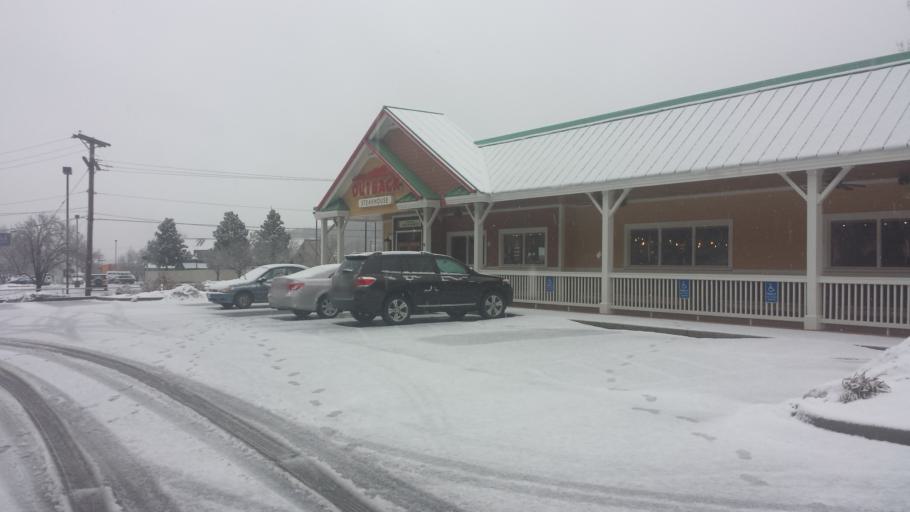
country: US
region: Virginia
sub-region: Roanoke County
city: Narrows
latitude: 37.2208
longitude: -79.9667
